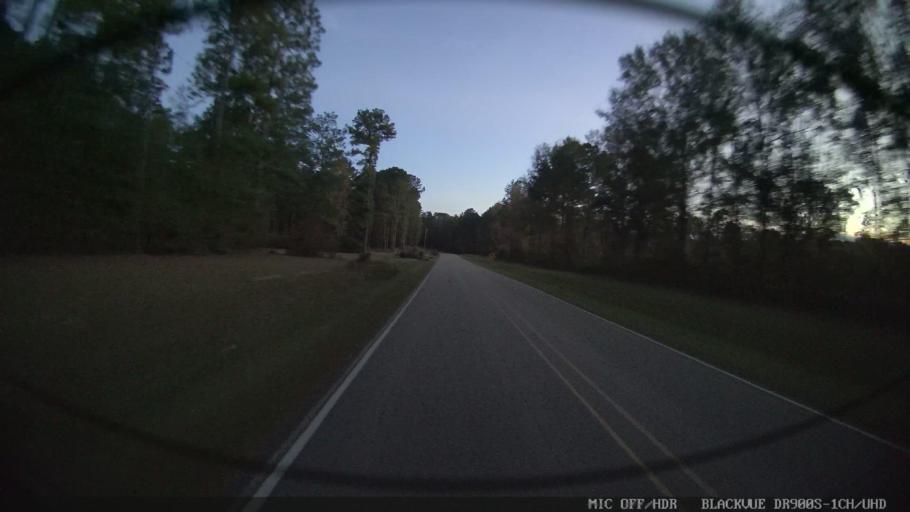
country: US
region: Mississippi
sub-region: Perry County
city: New Augusta
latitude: 31.1583
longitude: -89.2113
